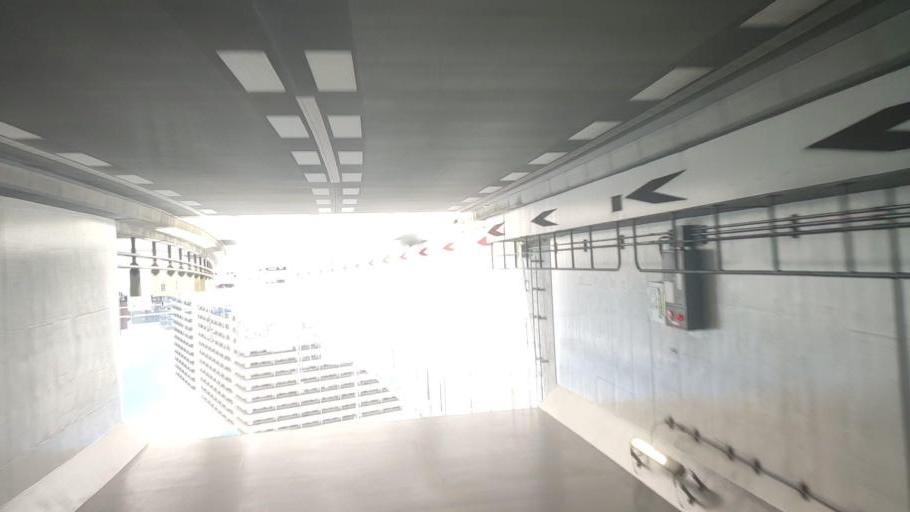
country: JP
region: Aichi
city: Nagoya-shi
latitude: 35.1628
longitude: 136.8805
